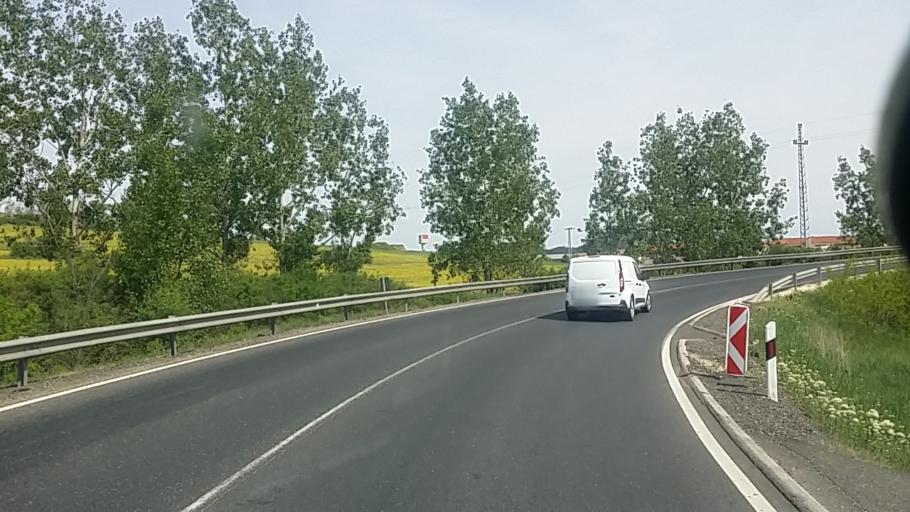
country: HU
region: Pest
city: Toeroekbalint
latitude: 47.4673
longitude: 18.8809
